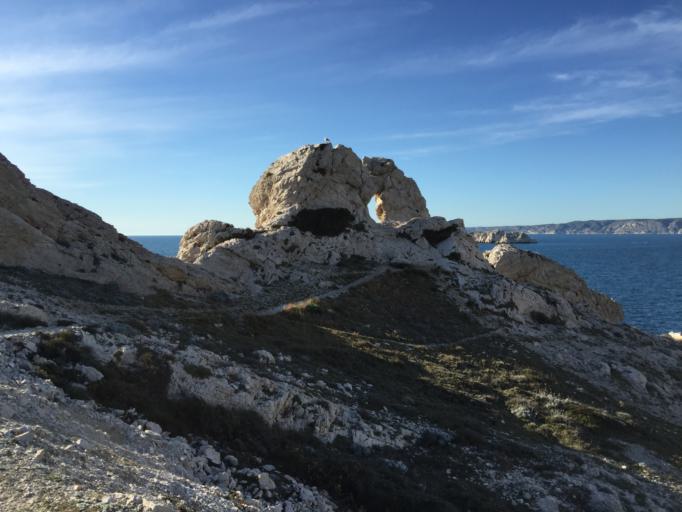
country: FR
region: Provence-Alpes-Cote d'Azur
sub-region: Departement des Bouches-du-Rhone
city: Marseille 07
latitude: 43.2711
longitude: 5.2988
